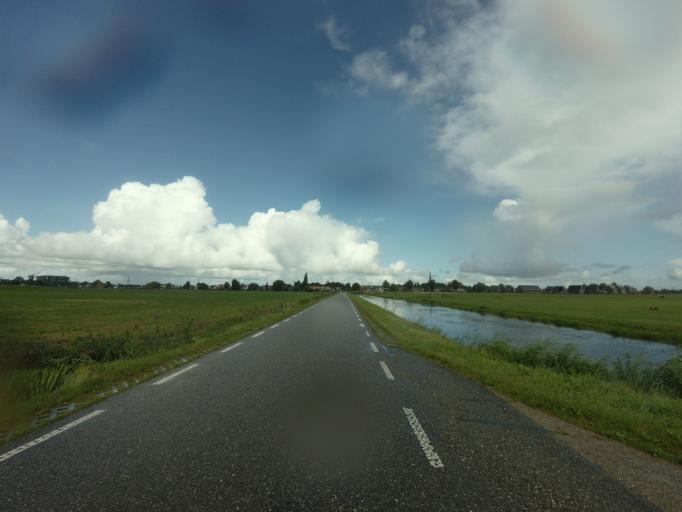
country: NL
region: Friesland
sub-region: Gemeente Leeuwarden
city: Wirdum
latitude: 53.1440
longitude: 5.8034
